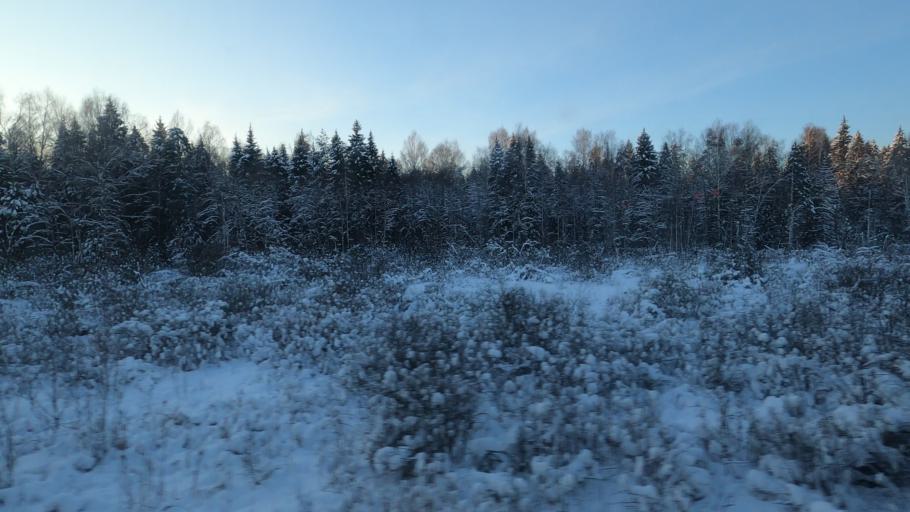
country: RU
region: Moskovskaya
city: Novo-Nikol'skoye
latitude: 56.5592
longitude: 37.5656
